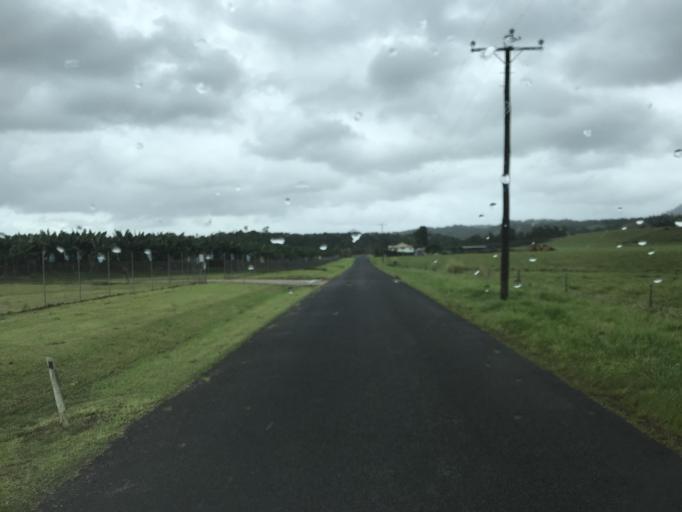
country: AU
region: Queensland
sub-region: Cassowary Coast
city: Innisfail
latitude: -17.5189
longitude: 145.9658
